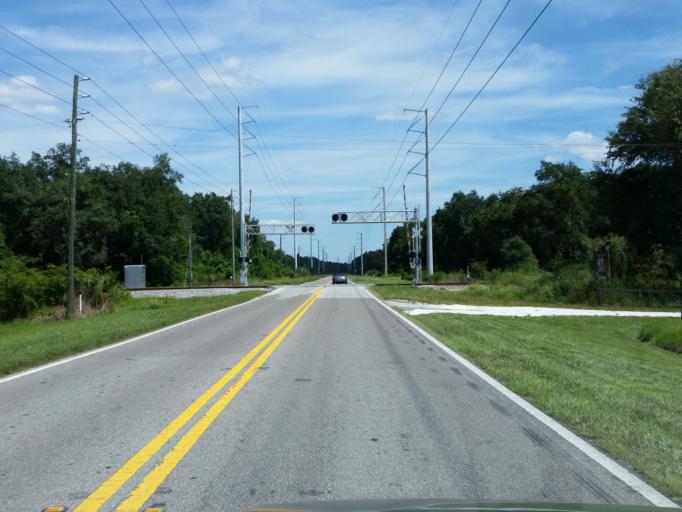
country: US
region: Florida
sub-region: Pasco County
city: Zephyrhills North
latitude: 28.2544
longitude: -82.1324
